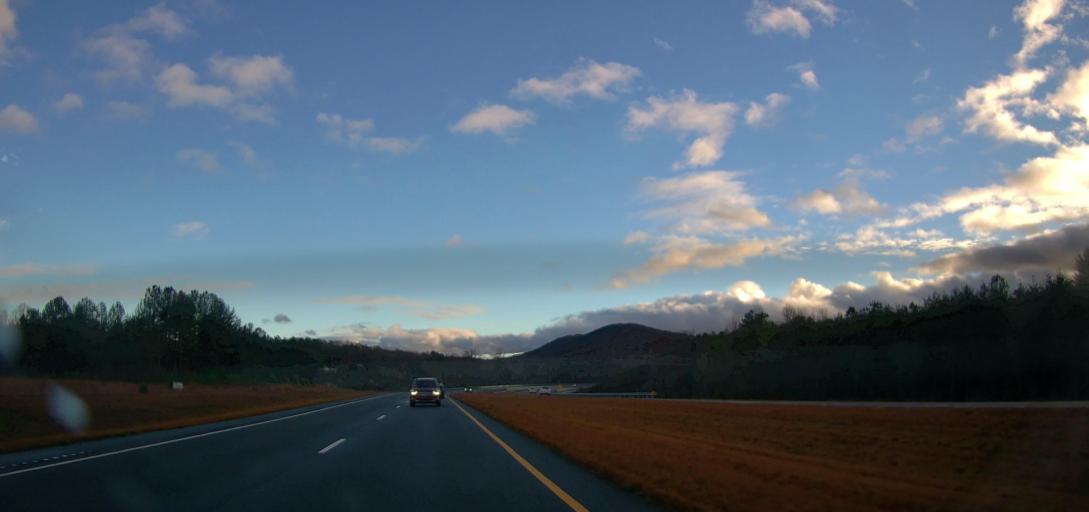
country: US
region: Georgia
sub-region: White County
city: Cleveland
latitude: 34.6027
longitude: -83.7816
